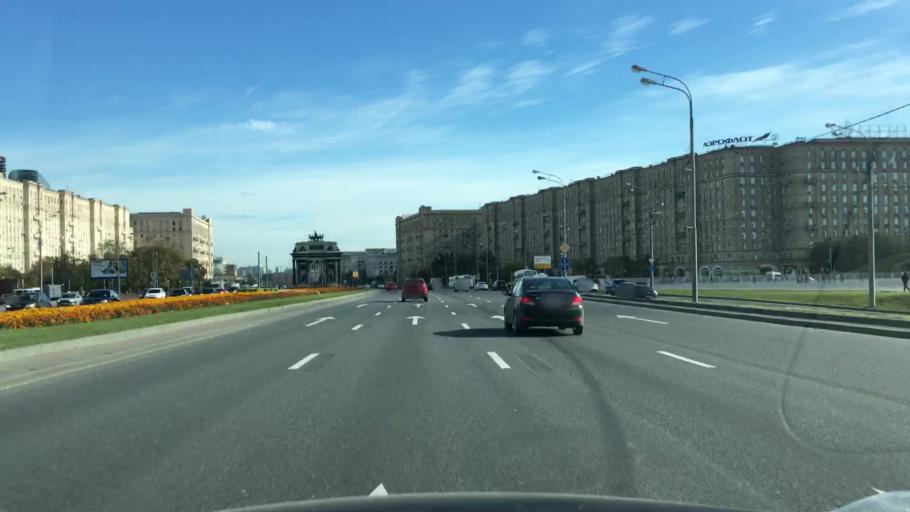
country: RU
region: Moskovskaya
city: Kastanayevo
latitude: 55.7352
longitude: 37.5138
